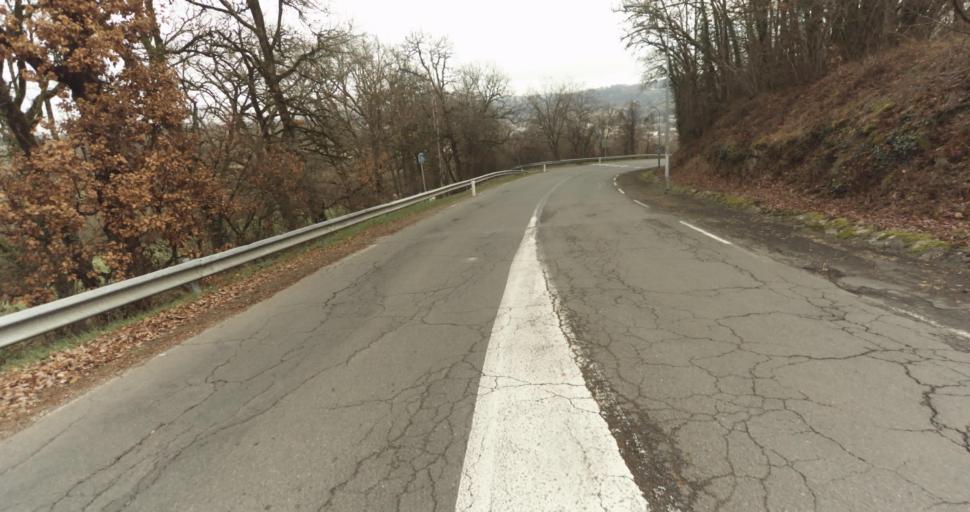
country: FR
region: Midi-Pyrenees
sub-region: Departement du Lot
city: Figeac
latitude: 44.6140
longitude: 2.0113
